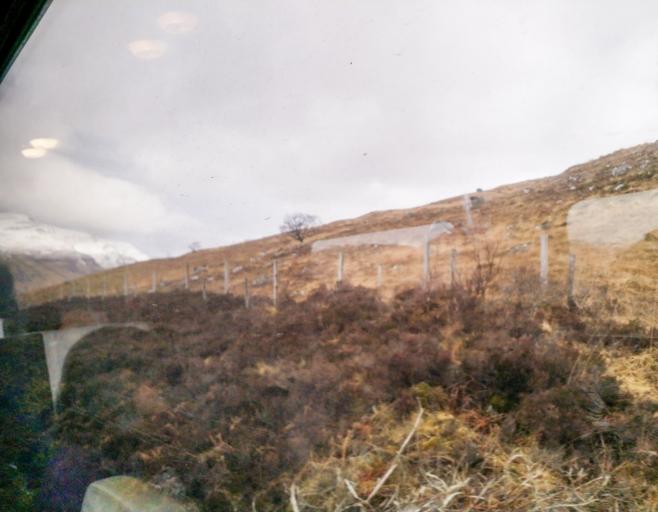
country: GB
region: Scotland
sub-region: Highland
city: Spean Bridge
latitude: 56.7783
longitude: -4.7319
